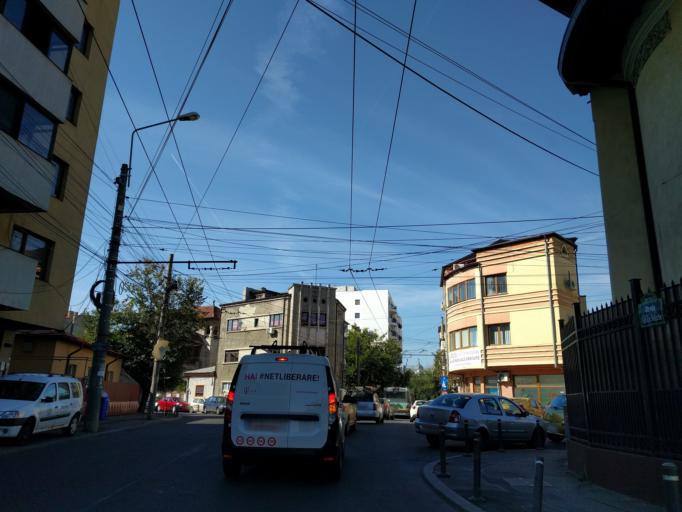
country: RO
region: Bucuresti
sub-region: Municipiul Bucuresti
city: Bucharest
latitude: 44.4341
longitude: 26.1271
